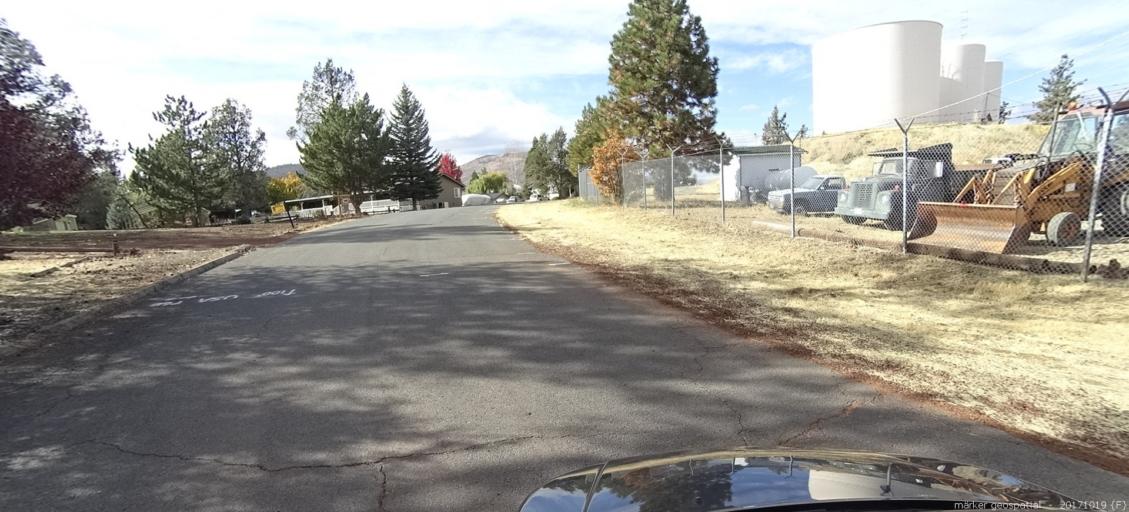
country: US
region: California
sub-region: Shasta County
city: Burney
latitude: 40.9995
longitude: -121.4468
